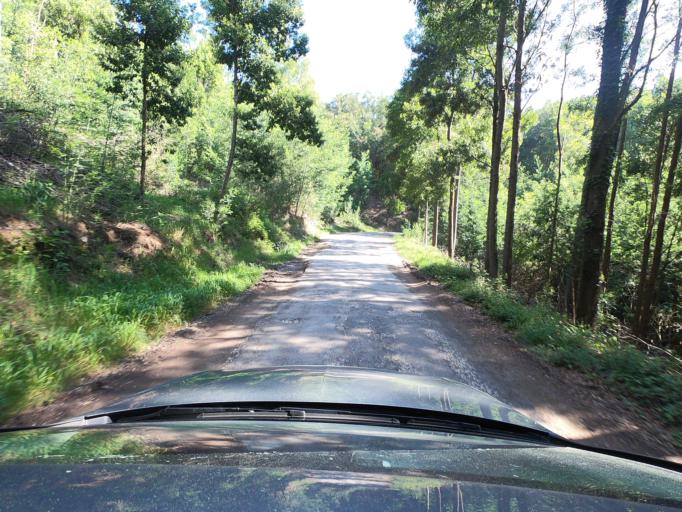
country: PT
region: Lisbon
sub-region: Sintra
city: Colares
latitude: 38.7781
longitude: -9.4374
